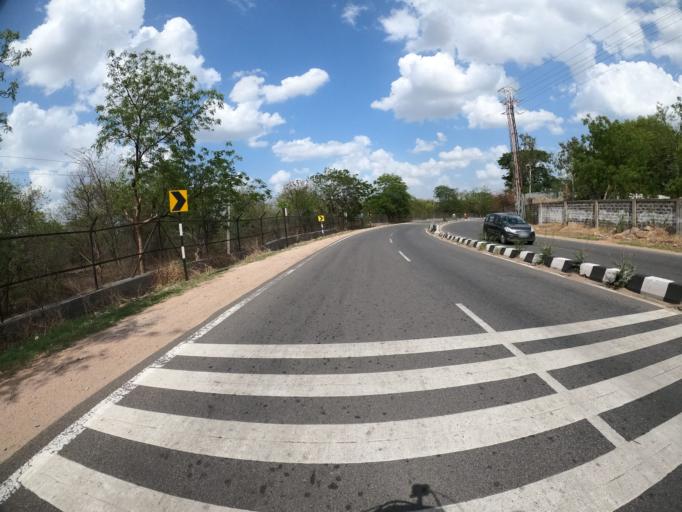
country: IN
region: Telangana
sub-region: Hyderabad
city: Hyderabad
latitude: 17.3538
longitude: 78.3429
